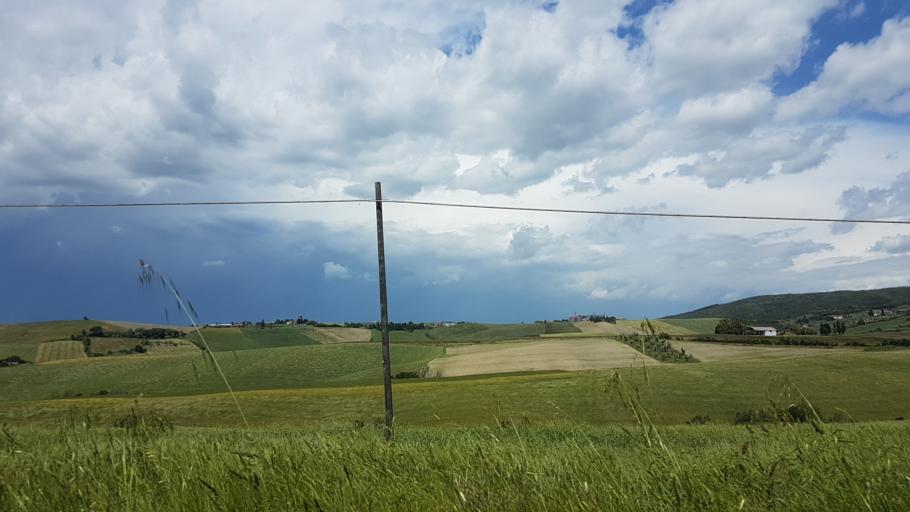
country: IT
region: Tuscany
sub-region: Province of Pisa
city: Santa Luce
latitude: 43.4677
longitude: 10.5535
